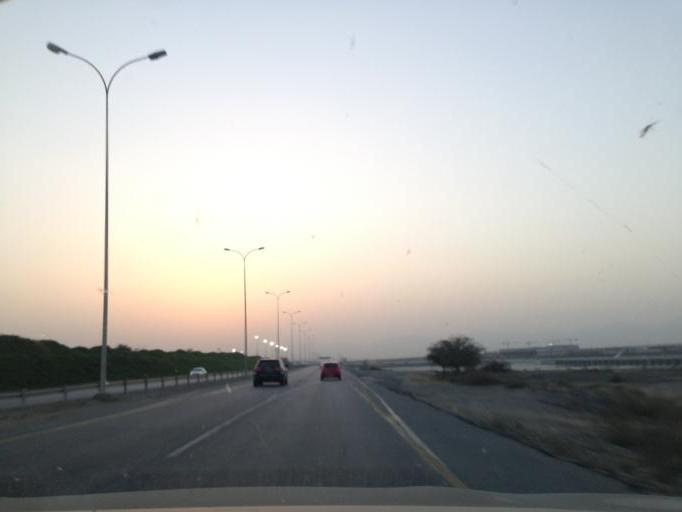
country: OM
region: Muhafazat Masqat
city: Bawshar
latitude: 23.6133
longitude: 58.2960
